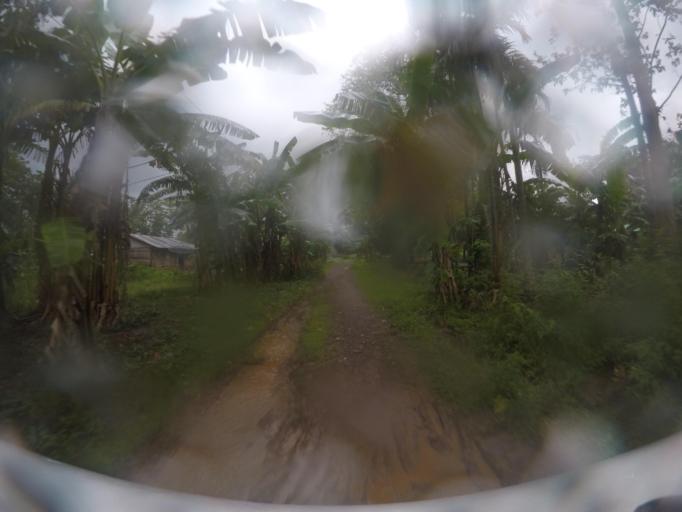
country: TL
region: Bobonaro
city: Maliana
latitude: -8.9637
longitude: 125.2149
